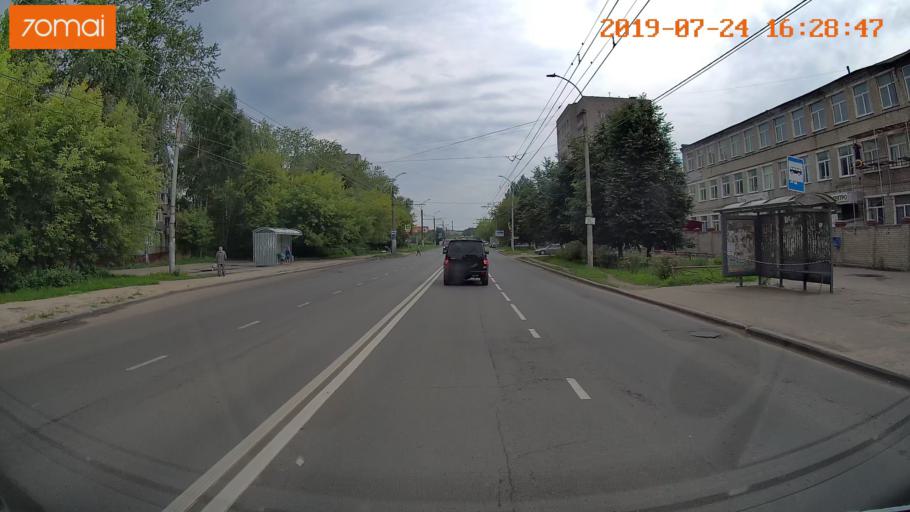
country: RU
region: Ivanovo
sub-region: Gorod Ivanovo
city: Ivanovo
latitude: 56.9682
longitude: 40.9630
